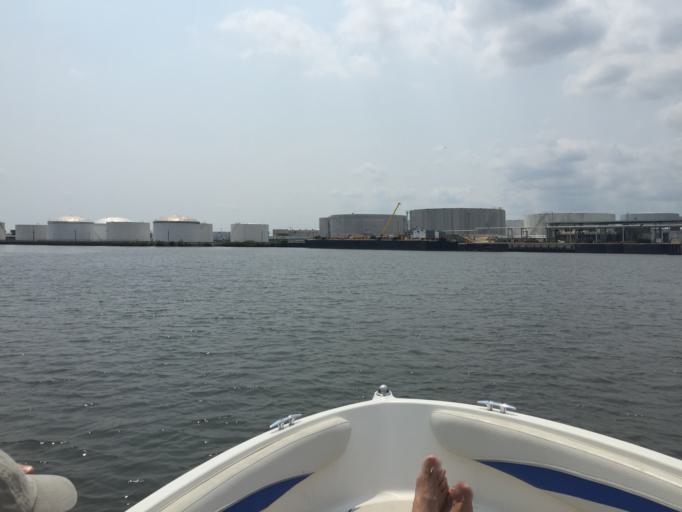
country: US
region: Pennsylvania
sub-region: Delaware County
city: Colwyn
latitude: 39.9106
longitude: -75.2132
